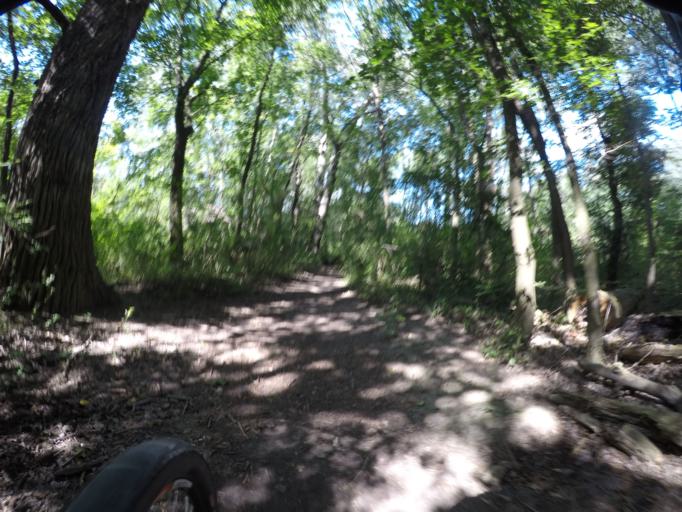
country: AT
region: Lower Austria
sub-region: Politischer Bezirk Wien-Umgebung
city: Schwechat
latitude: 48.1847
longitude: 16.4889
